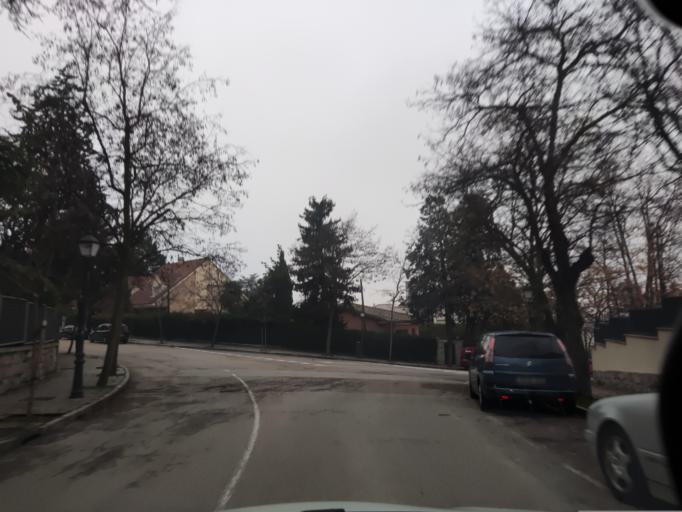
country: ES
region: Madrid
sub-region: Provincia de Madrid
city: Tetuan de las Victorias
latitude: 40.4871
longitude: -3.7103
